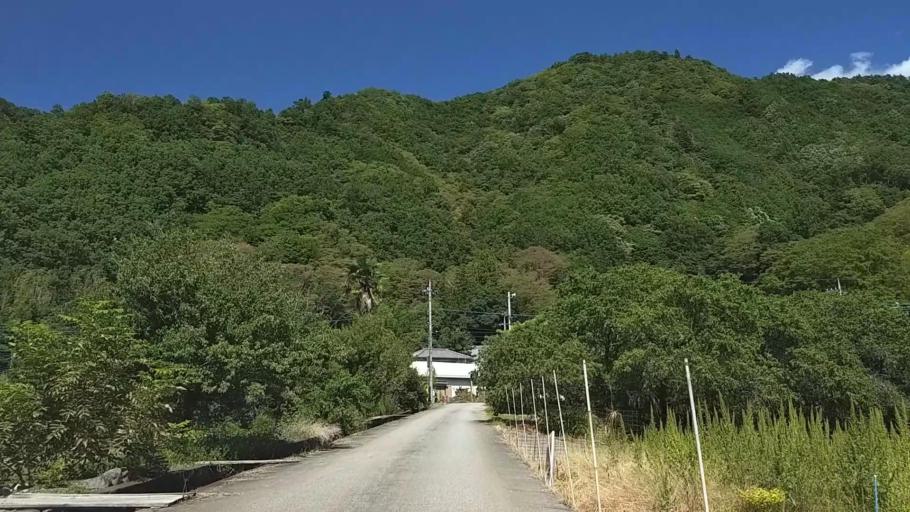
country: JP
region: Yamanashi
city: Ryuo
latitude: 35.5123
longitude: 138.4617
